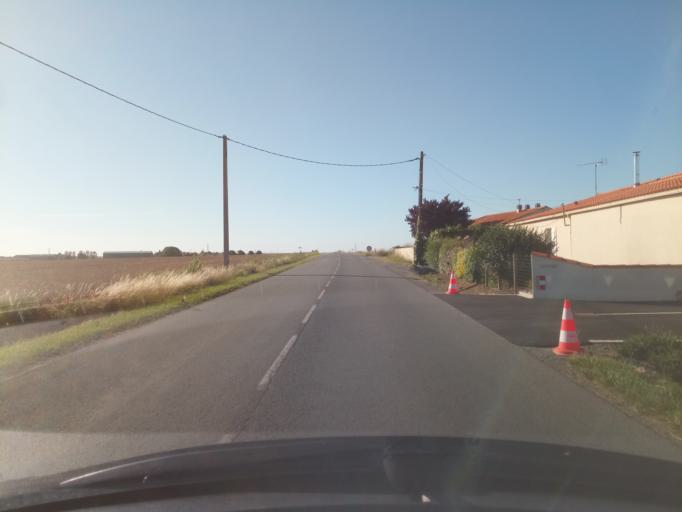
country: FR
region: Poitou-Charentes
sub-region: Departement de la Charente-Maritime
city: Marans
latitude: 46.3013
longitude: -0.9824
